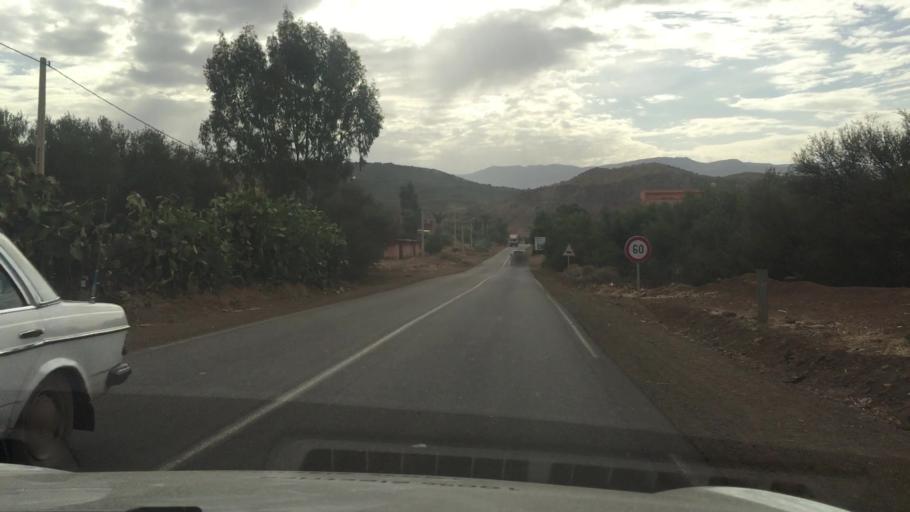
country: MA
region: Marrakech-Tensift-Al Haouz
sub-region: Al-Haouz
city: Touama
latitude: 31.5487
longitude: -7.5761
